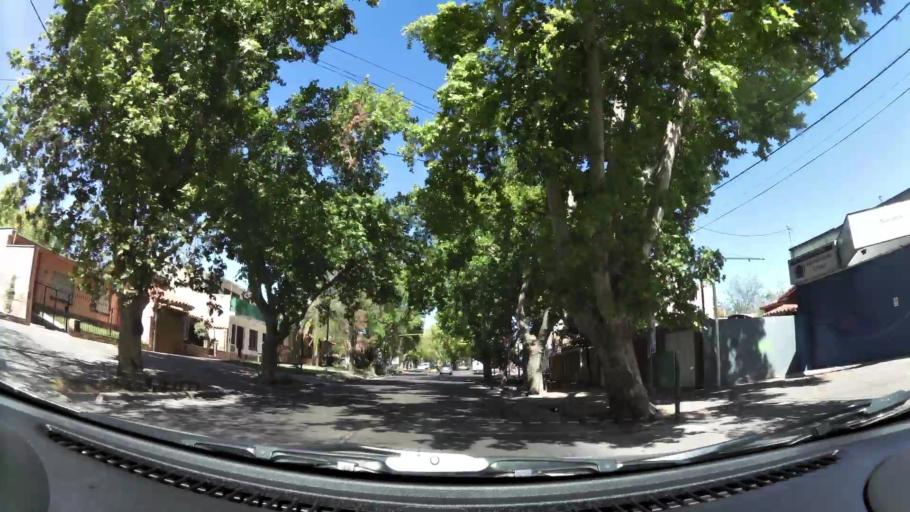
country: AR
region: Mendoza
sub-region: Departamento de Godoy Cruz
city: Godoy Cruz
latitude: -32.9554
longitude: -68.8497
